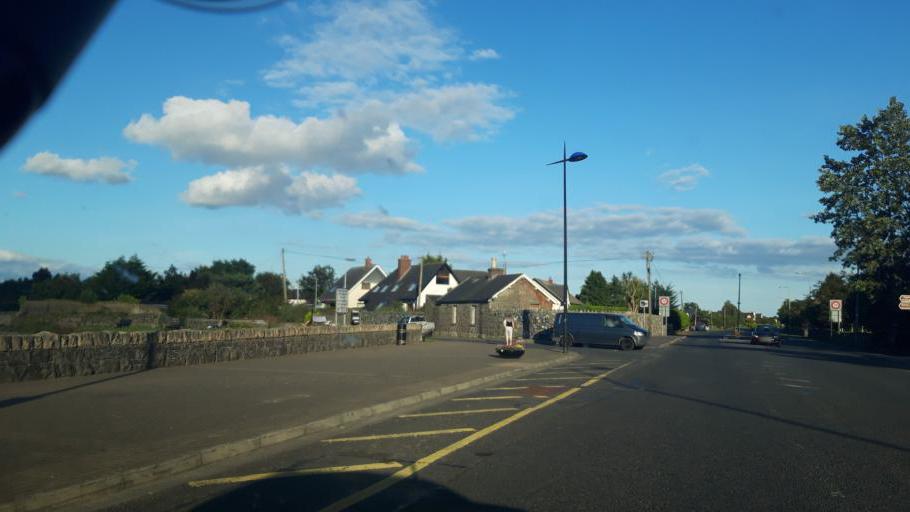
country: IE
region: Leinster
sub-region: Lu
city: Carlingford
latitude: 54.0401
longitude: -6.1830
